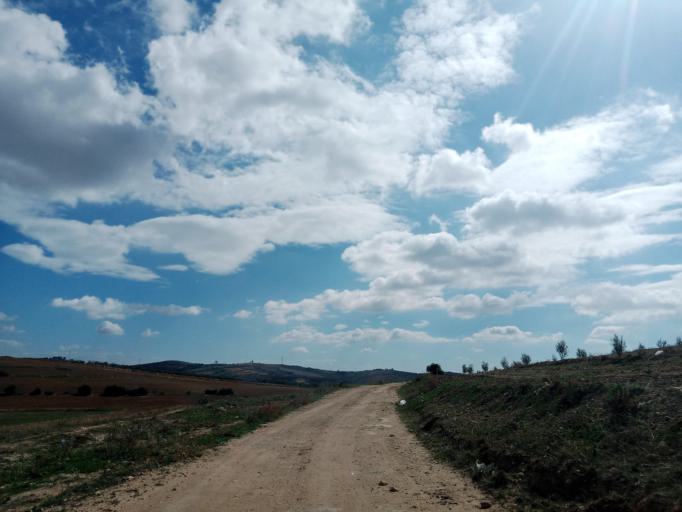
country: TN
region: Tunis
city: Oued Lill
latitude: 36.8090
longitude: 9.9839
